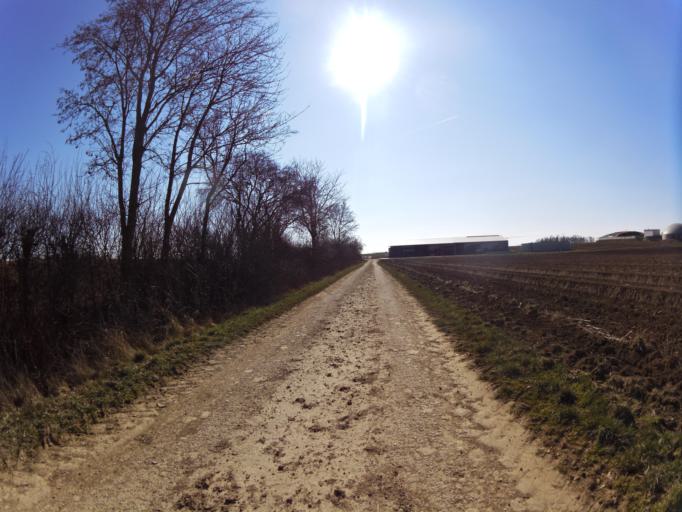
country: DE
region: Bavaria
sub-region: Regierungsbezirk Unterfranken
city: Unterpleichfeld
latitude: 49.8695
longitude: 10.0594
